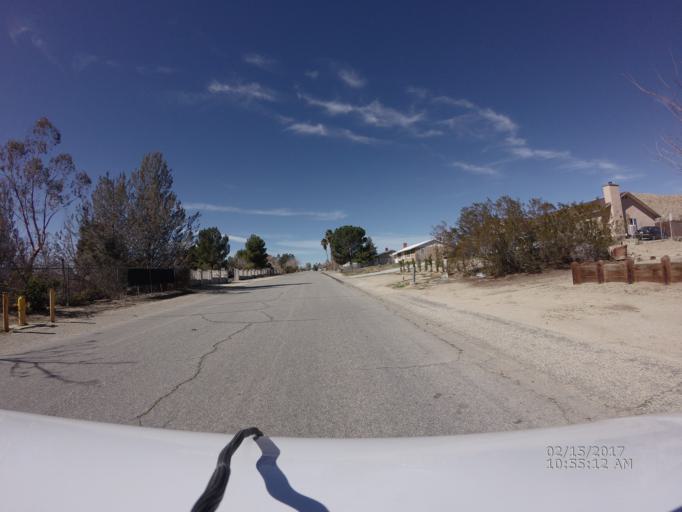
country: US
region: California
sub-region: Los Angeles County
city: Lake Los Angeles
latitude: 34.5860
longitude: -117.8475
